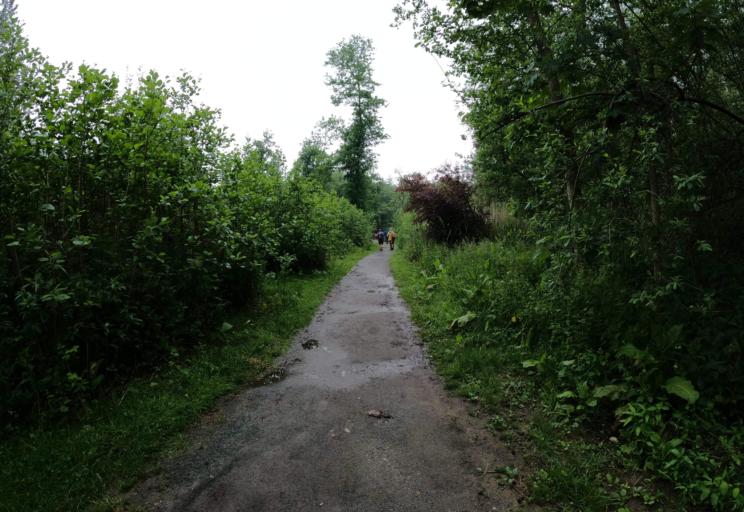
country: BE
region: Flanders
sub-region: Provincie Oost-Vlaanderen
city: Berlare
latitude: 51.0337
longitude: 4.0009
